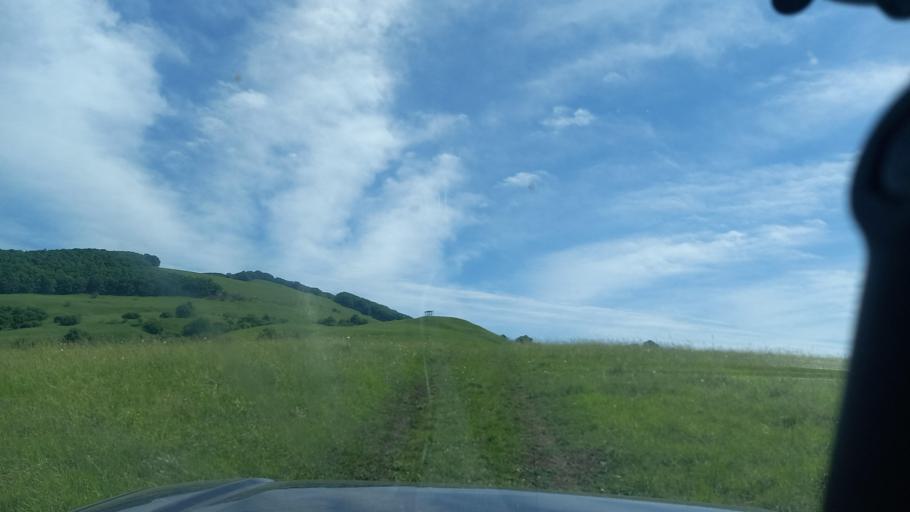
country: RU
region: Karachayevo-Cherkesiya
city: Kurdzhinovo
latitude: 44.1436
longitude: 41.0607
